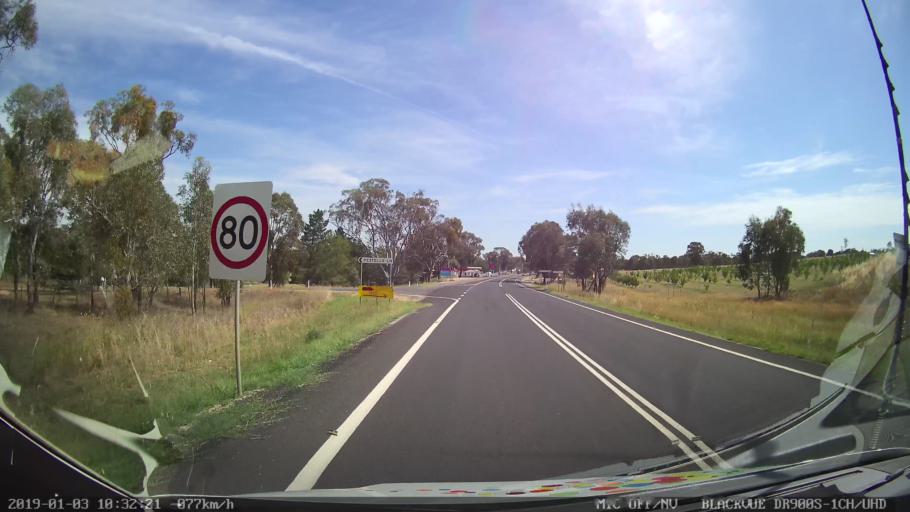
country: AU
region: New South Wales
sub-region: Young
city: Young
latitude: -34.3398
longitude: 148.2828
